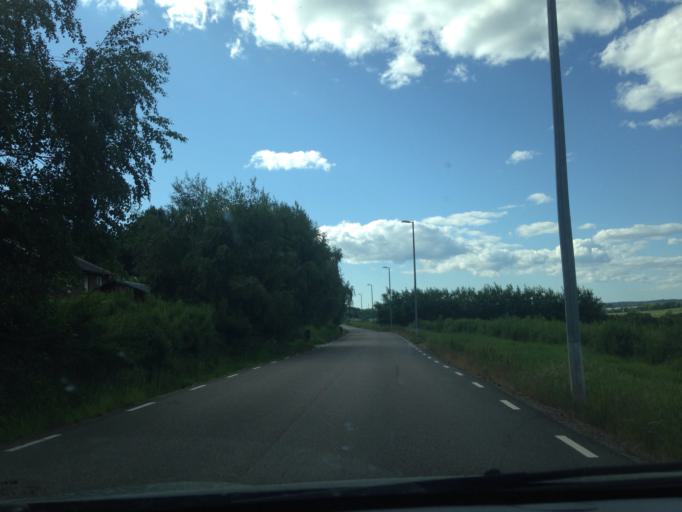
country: SE
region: Vaestra Goetaland
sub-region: Goteborg
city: Goeteborg
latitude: 57.7863
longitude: 11.9308
